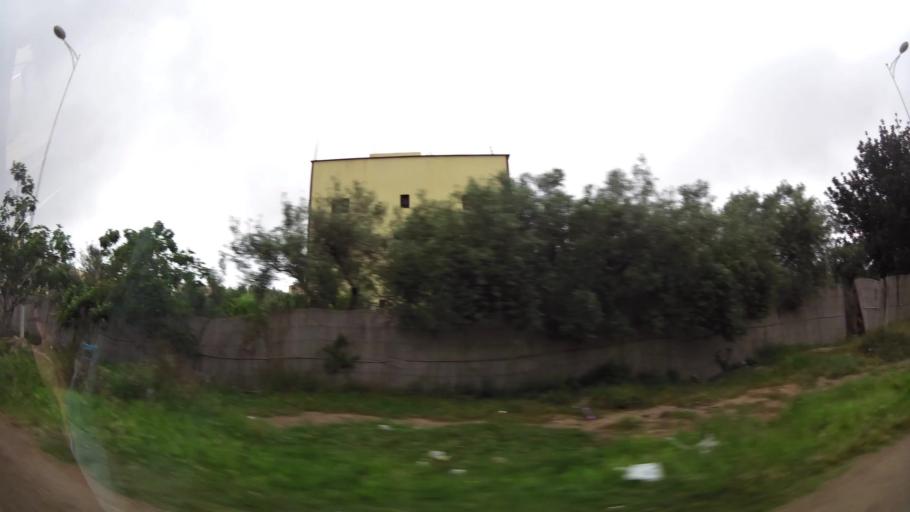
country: MA
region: Oriental
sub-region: Nador
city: Midar
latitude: 35.0549
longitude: -3.4628
